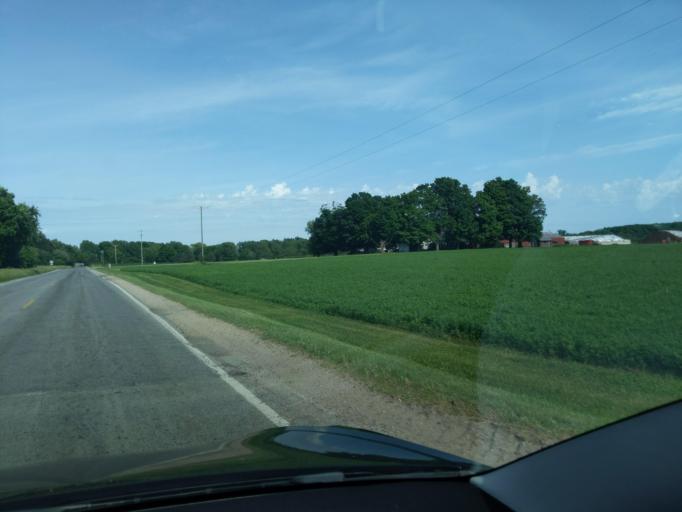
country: US
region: Michigan
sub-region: Newaygo County
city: Fremont
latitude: 43.4238
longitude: -85.9798
